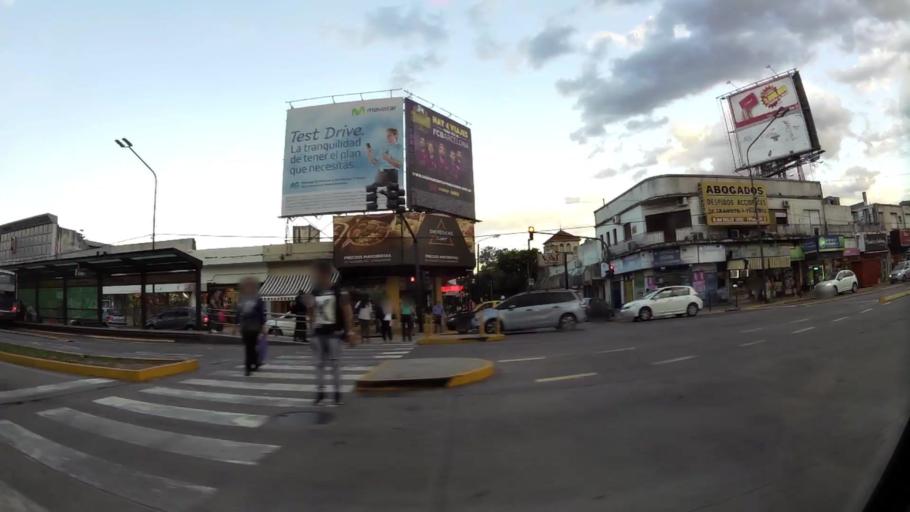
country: AR
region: Buenos Aires
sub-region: Partido de Vicente Lopez
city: Olivos
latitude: -34.5363
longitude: -58.4773
